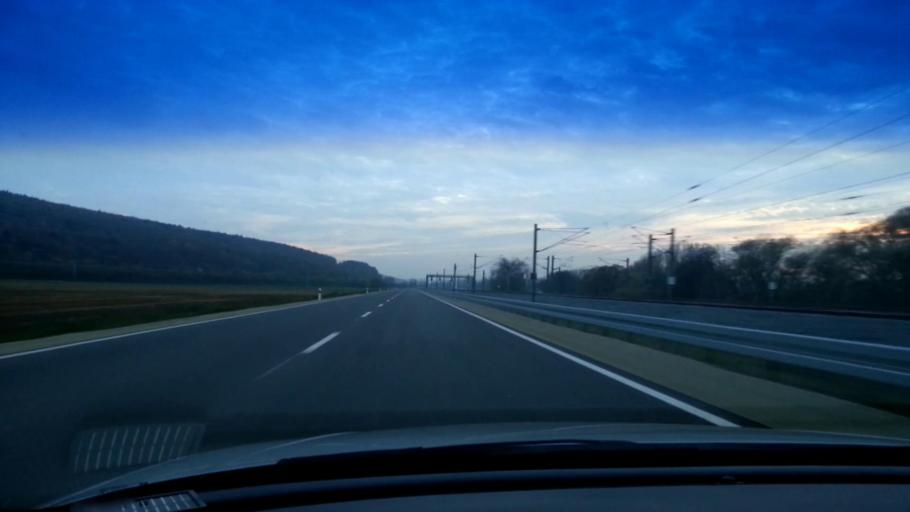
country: DE
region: Bavaria
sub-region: Upper Franconia
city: Zapfendorf
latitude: 50.0058
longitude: 10.9185
